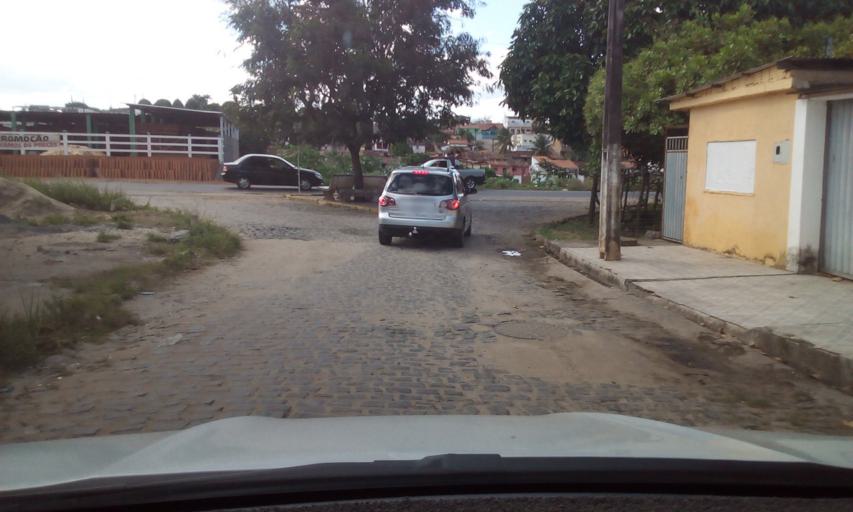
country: BR
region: Paraiba
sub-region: Guarabira
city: Guarabira
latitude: -6.8669
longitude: -35.4878
